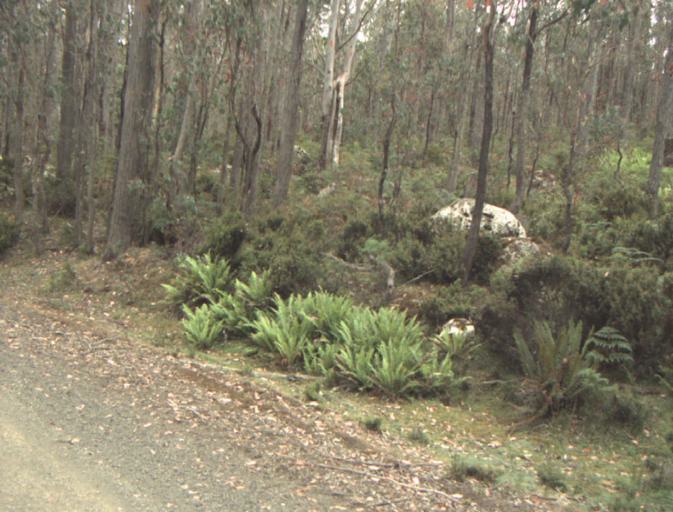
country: AU
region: Tasmania
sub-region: Northern Midlands
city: Evandale
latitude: -41.4982
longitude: 147.5836
